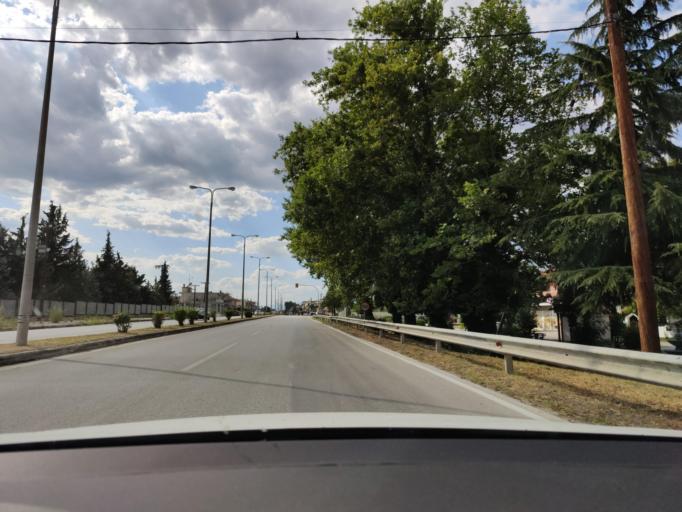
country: GR
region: Central Macedonia
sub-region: Nomos Serron
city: Lefkonas
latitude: 41.0949
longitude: 23.5041
